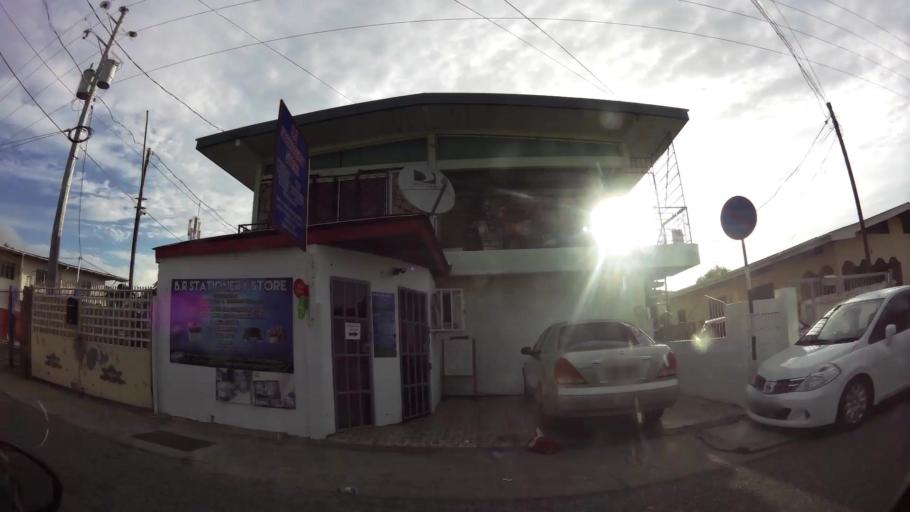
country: TT
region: Tunapuna/Piarco
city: Tunapuna
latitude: 10.6391
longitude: -61.4028
